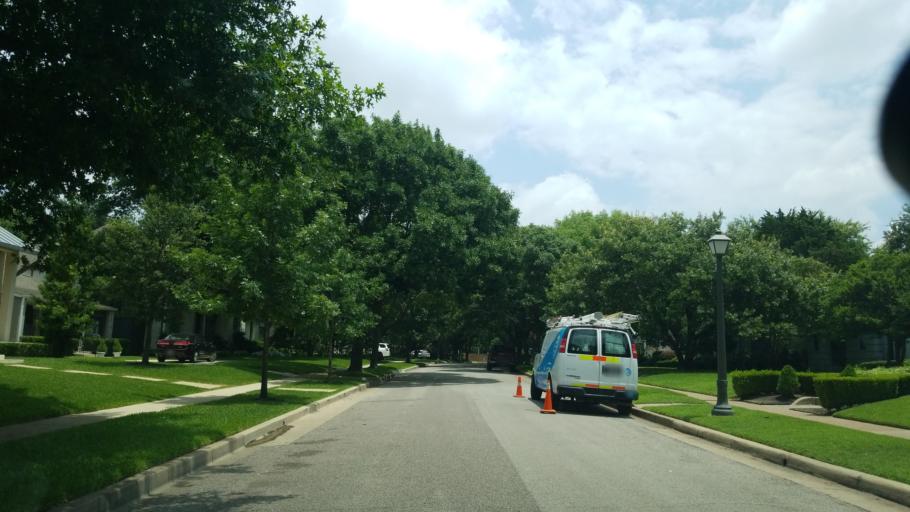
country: US
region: Texas
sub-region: Dallas County
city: University Park
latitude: 32.8349
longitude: -96.8174
